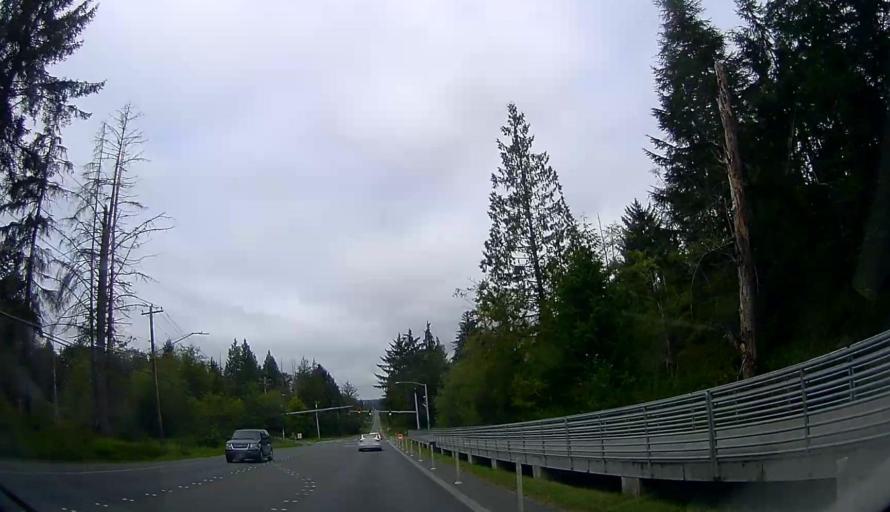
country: US
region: Washington
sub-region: Snohomish County
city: Tulalip
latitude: 48.0537
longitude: -122.2617
